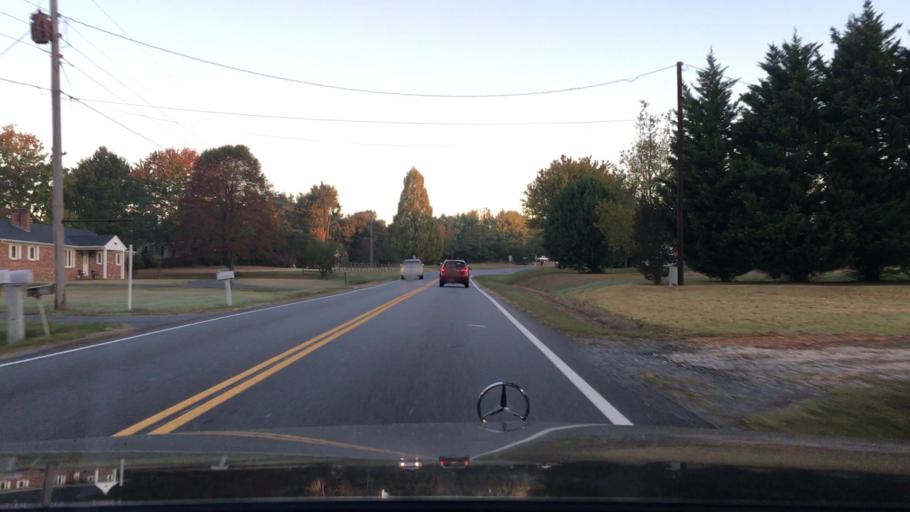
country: US
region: Virginia
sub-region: Campbell County
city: Timberlake
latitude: 37.3140
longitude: -79.2385
